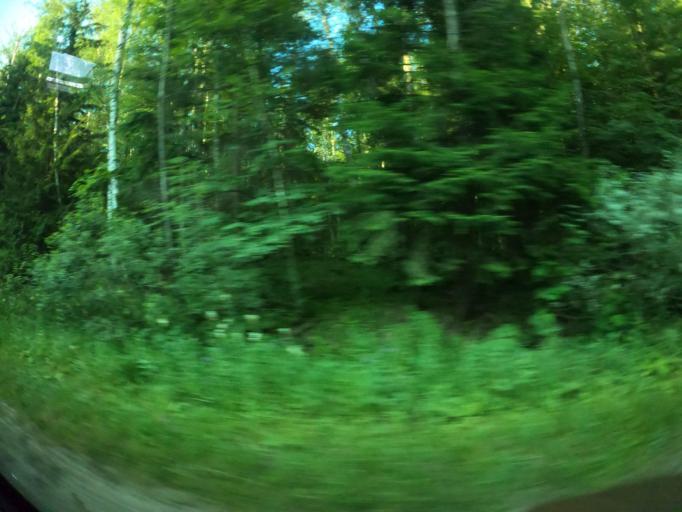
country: RU
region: Moskovskaya
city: Obolensk
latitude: 54.9860
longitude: 37.2103
